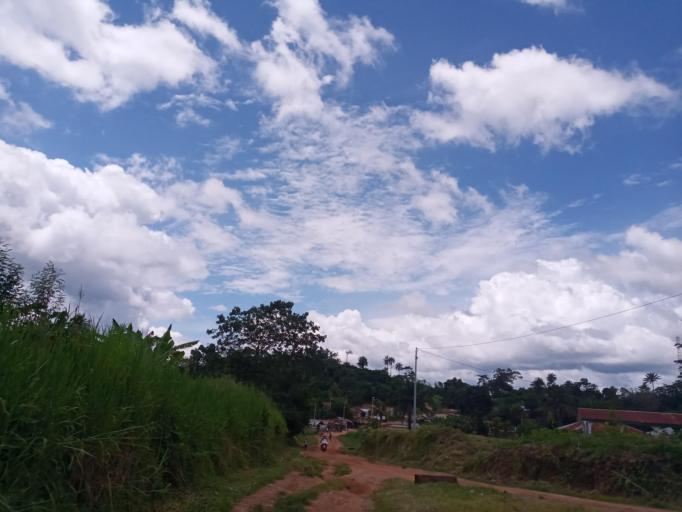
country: SL
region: Eastern Province
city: Tombu
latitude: 8.6261
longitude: -10.8241
